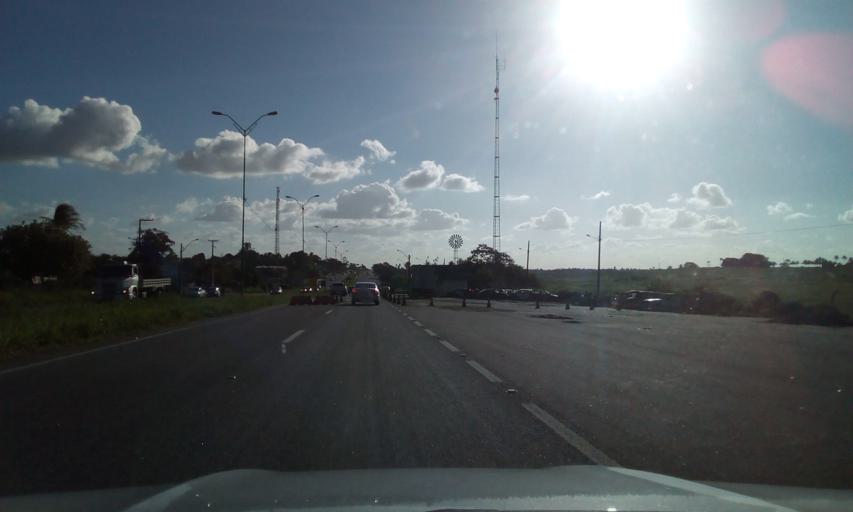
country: BR
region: Paraiba
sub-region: Pilar
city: Pilar
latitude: -7.1919
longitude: -35.2250
